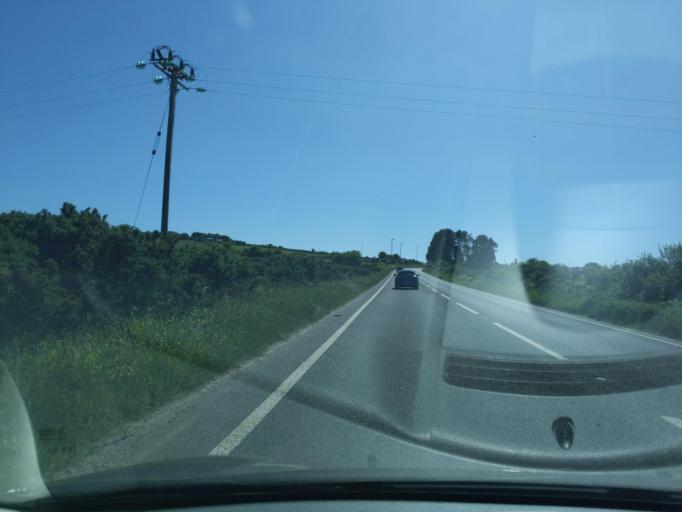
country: GB
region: England
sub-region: Cornwall
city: Penryn
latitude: 50.1657
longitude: -5.1528
